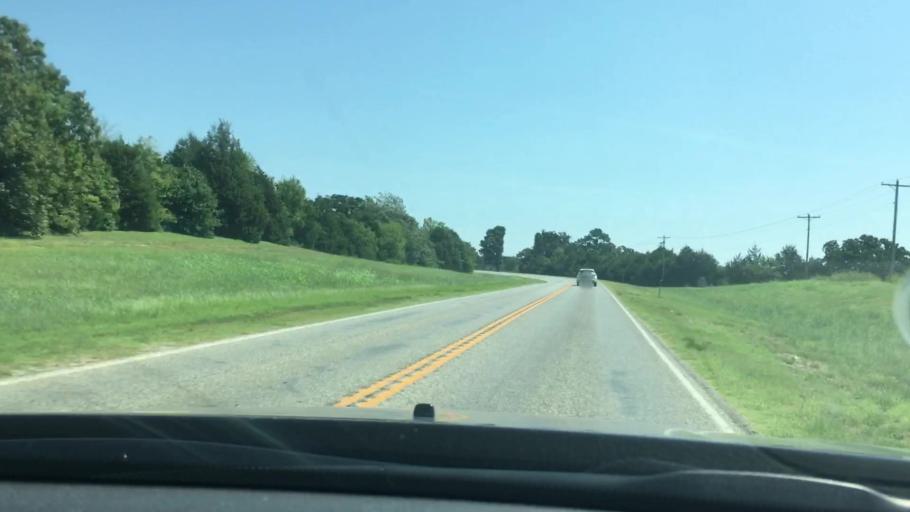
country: US
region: Oklahoma
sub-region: Johnston County
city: Tishomingo
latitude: 34.2305
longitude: -96.6293
